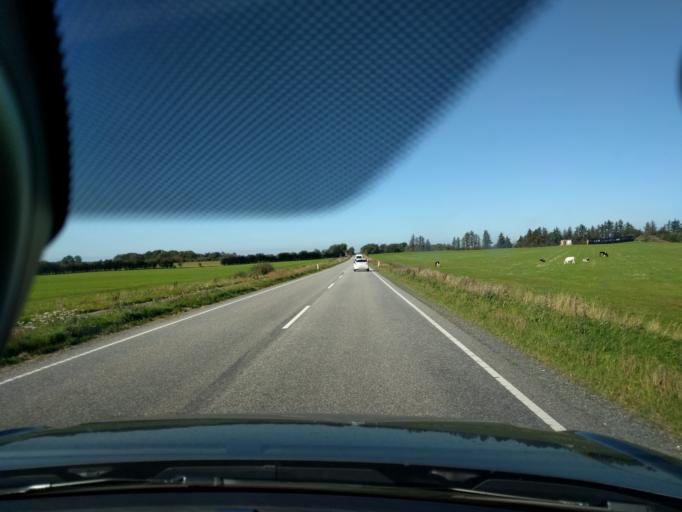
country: DK
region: North Denmark
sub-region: Mariagerfjord Kommune
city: Hobro
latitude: 56.6829
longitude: 9.6596
